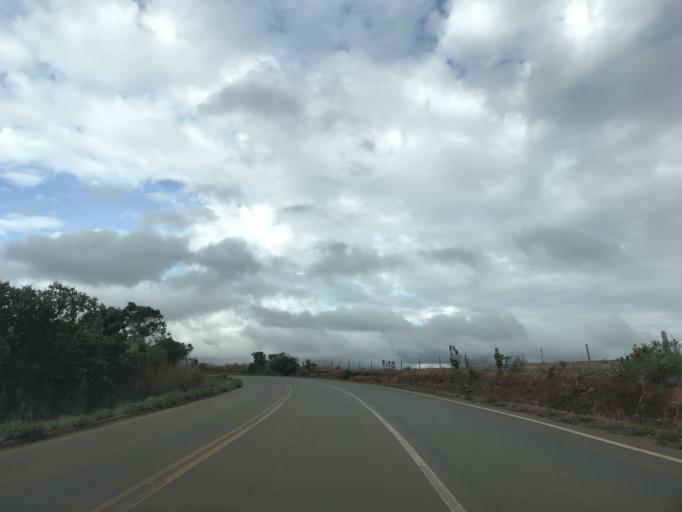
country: BR
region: Goias
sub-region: Vianopolis
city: Vianopolis
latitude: -16.5765
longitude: -48.2963
